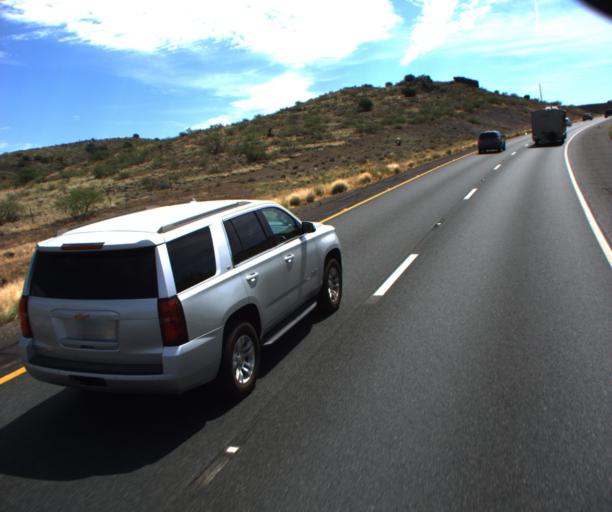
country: US
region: Arizona
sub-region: Yavapai County
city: Cordes Lakes
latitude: 34.4218
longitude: -112.0578
